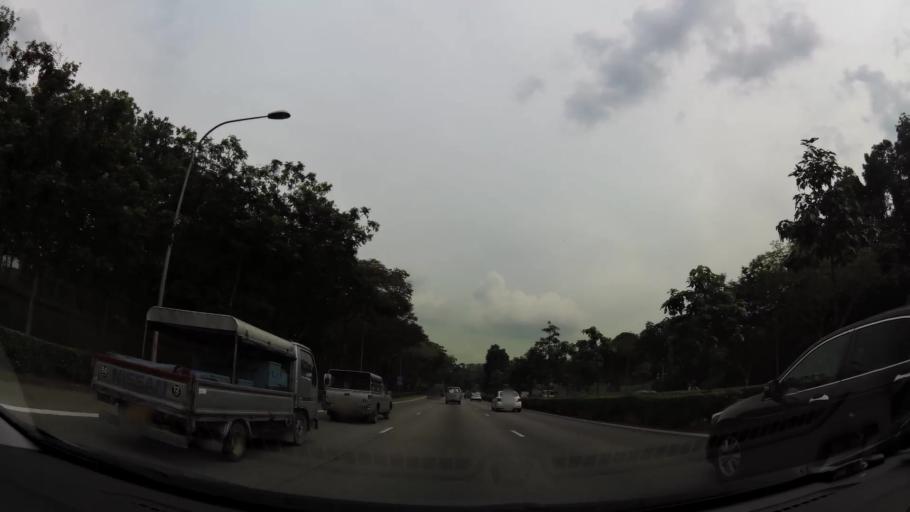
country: MY
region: Johor
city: Johor Bahru
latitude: 1.4167
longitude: 103.8036
